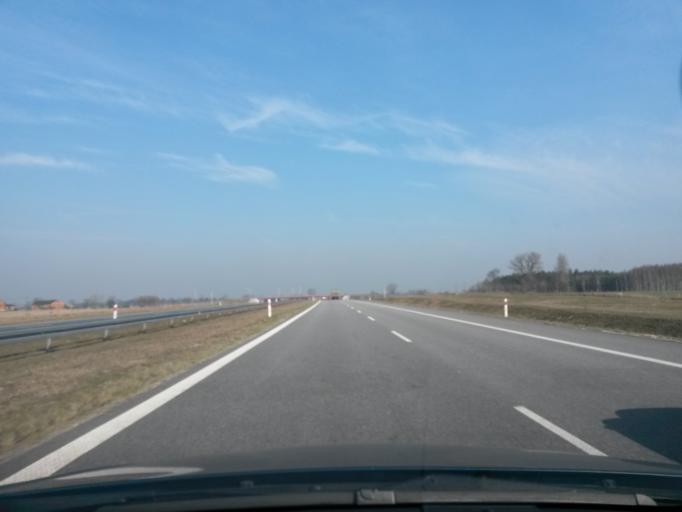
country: PL
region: Lodz Voivodeship
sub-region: Powiat kutnowski
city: Krzyzanow
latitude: 52.1945
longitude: 19.4874
